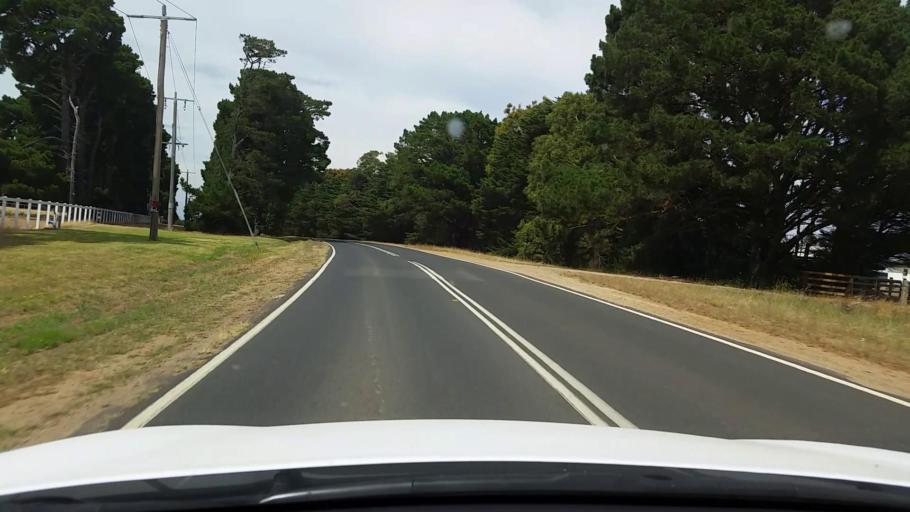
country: AU
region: Victoria
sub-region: Mornington Peninsula
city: Merricks
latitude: -38.4564
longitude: 145.0198
